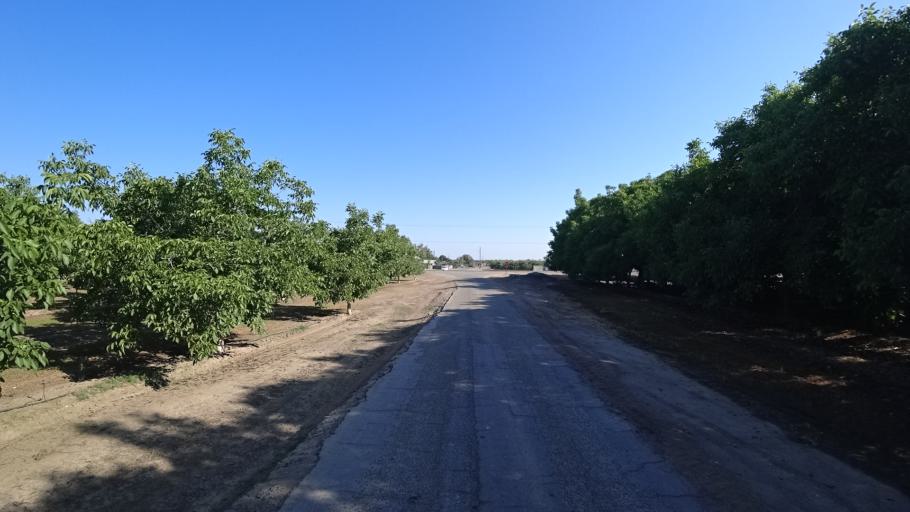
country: US
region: California
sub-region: Fresno County
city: Laton
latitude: 36.4004
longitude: -119.7182
